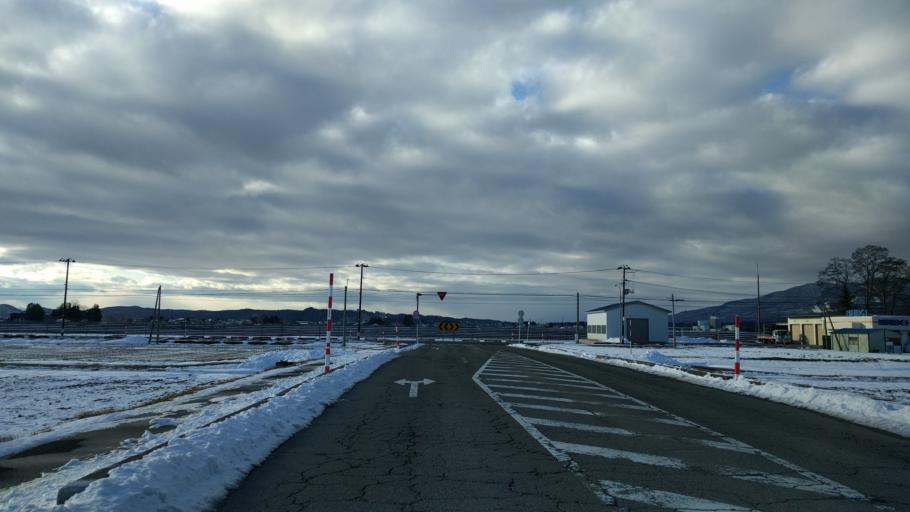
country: JP
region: Fukushima
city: Inawashiro
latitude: 37.5392
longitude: 140.1054
